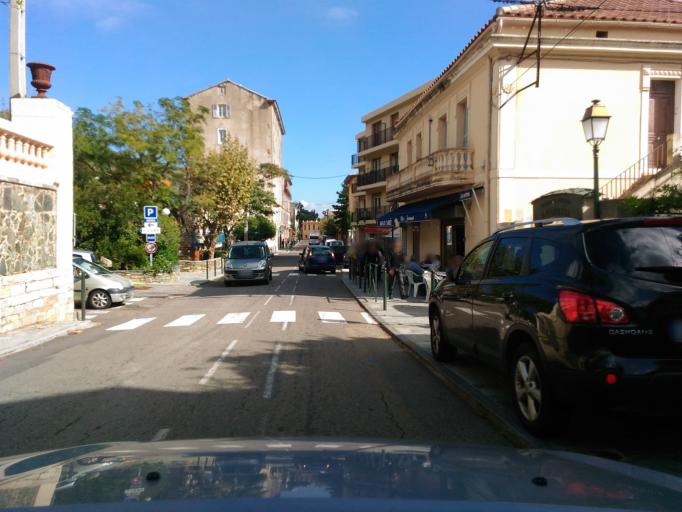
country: FR
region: Corsica
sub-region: Departement de la Haute-Corse
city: Brando
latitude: 42.7742
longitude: 9.4751
